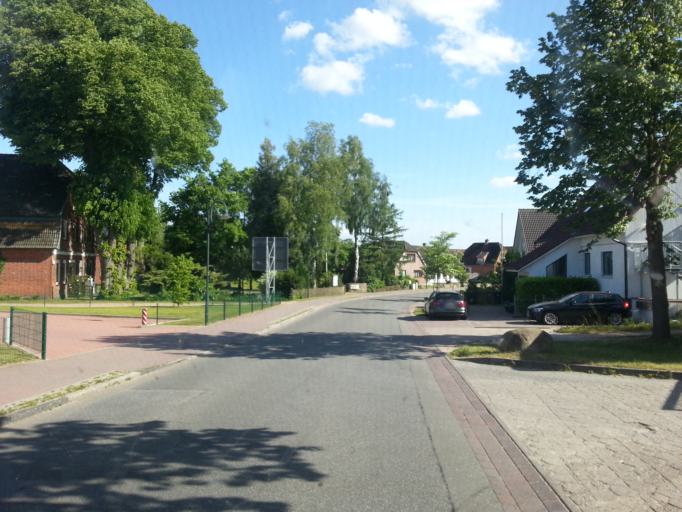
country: DE
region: Schleswig-Holstein
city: Scharbeutz
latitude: 54.0029
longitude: 10.7231
